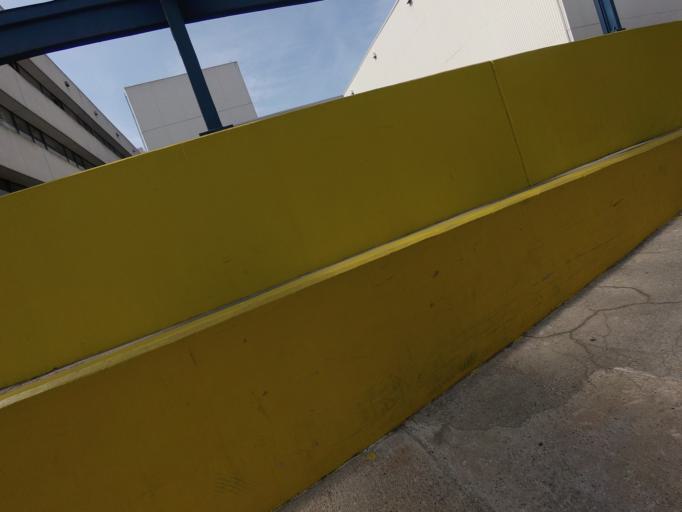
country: BE
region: Flanders
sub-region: Provincie Antwerpen
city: Aartselaar
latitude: 51.1598
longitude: 4.4072
